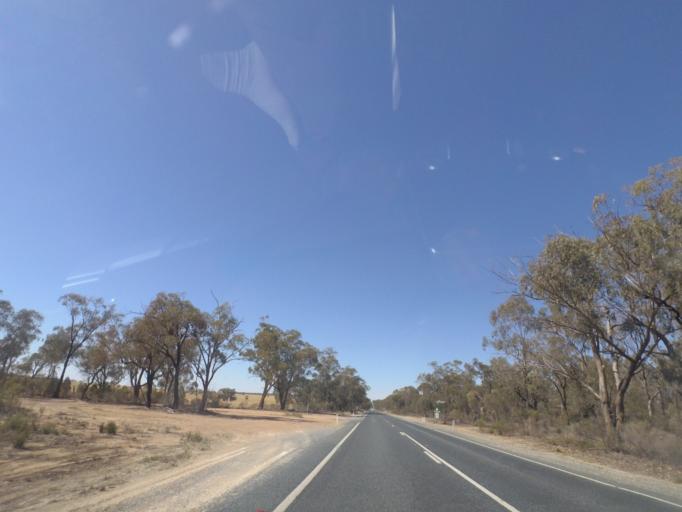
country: AU
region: New South Wales
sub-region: Bland
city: West Wyalong
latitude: -34.1423
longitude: 147.1199
